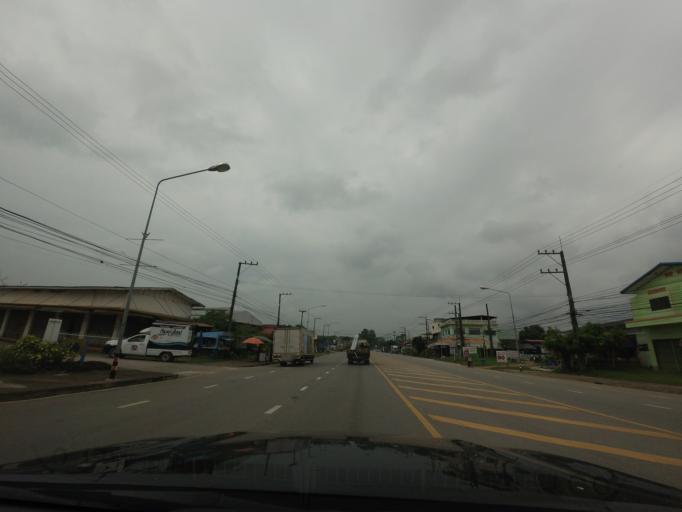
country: TH
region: Nong Khai
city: Si Chiang Mai
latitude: 17.9563
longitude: 102.5803
